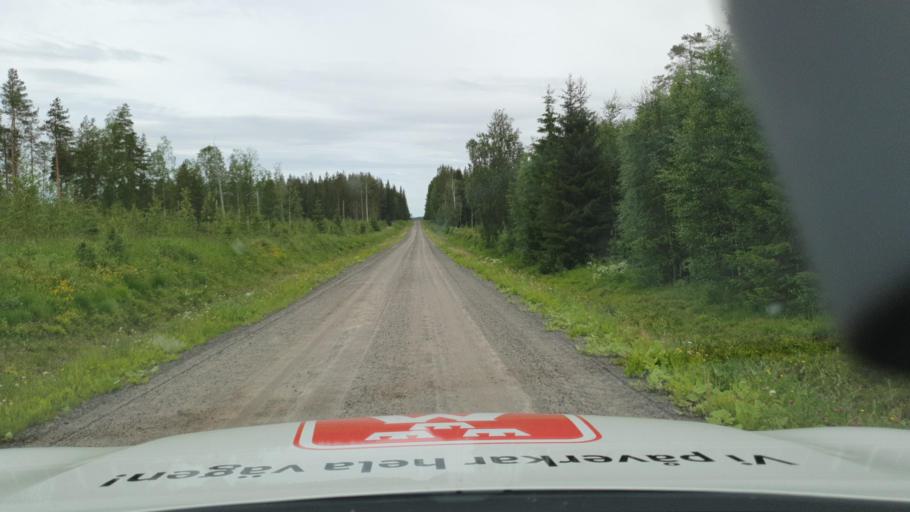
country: SE
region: Vaesterbotten
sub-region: Skelleftea Kommun
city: Burtraesk
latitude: 64.3737
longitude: 20.6157
